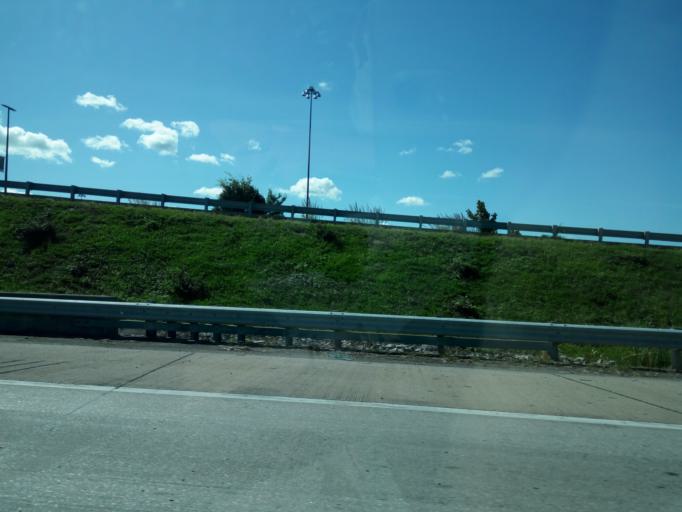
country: US
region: Kentucky
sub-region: Jefferson County
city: Audubon Park
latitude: 38.1893
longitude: -85.7422
